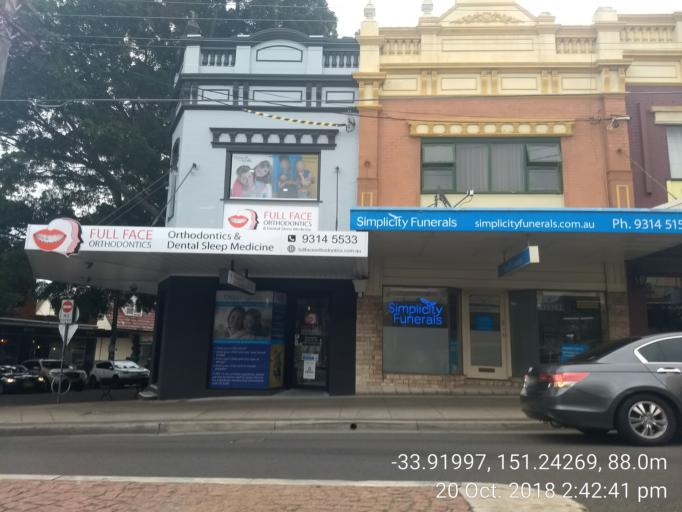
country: AU
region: New South Wales
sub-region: Randwick
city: Randwick
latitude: -33.9200
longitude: 151.2427
